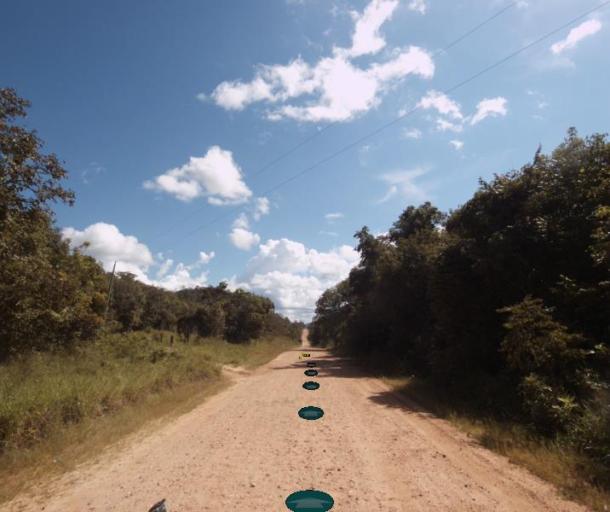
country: BR
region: Goias
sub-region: Pirenopolis
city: Pirenopolis
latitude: -15.7846
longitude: -49.0570
